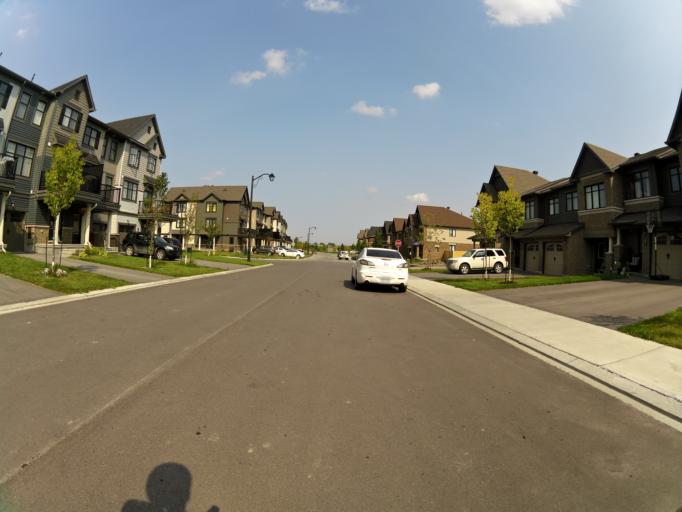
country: CA
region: Ontario
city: Bells Corners
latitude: 45.3039
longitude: -75.9372
